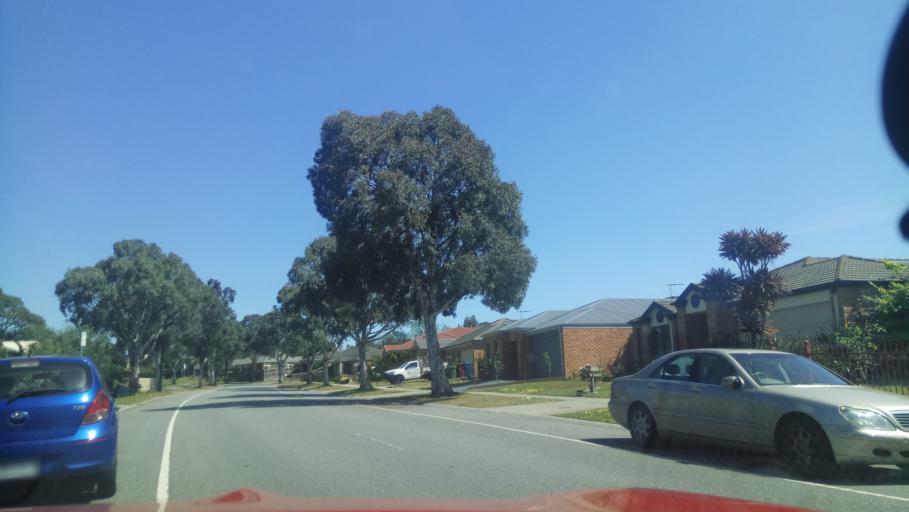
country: AU
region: Victoria
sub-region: Casey
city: Lynbrook
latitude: -38.0587
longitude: 145.2482
